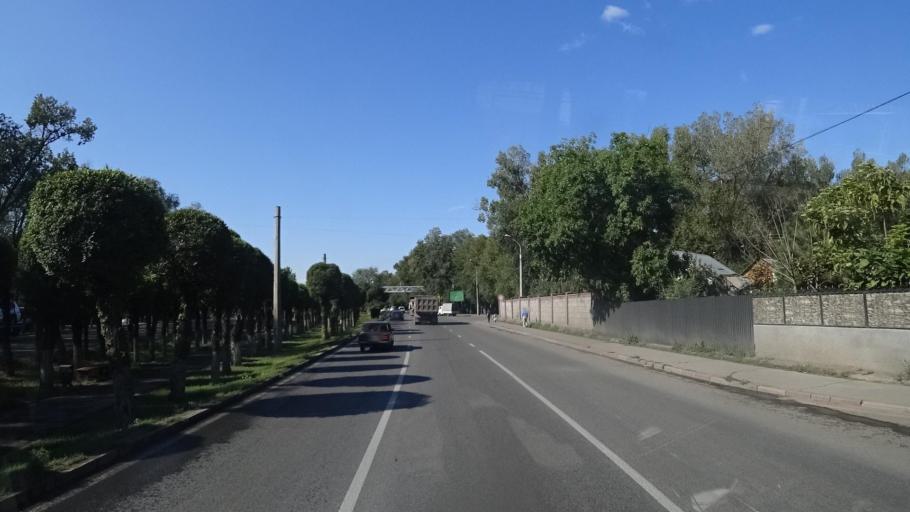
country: KZ
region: Almaty Oblysy
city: Pervomayskiy
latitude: 43.3445
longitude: 76.9912
